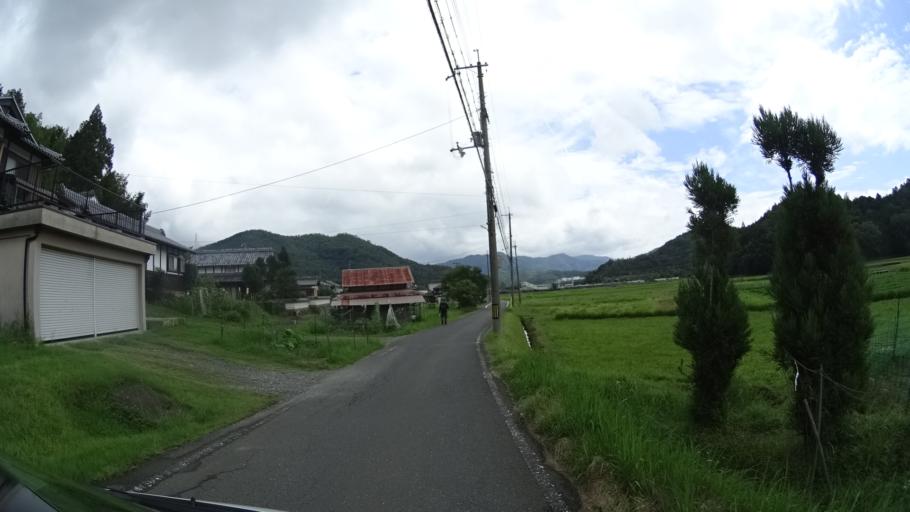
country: JP
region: Kyoto
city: Kameoka
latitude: 35.0902
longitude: 135.4944
